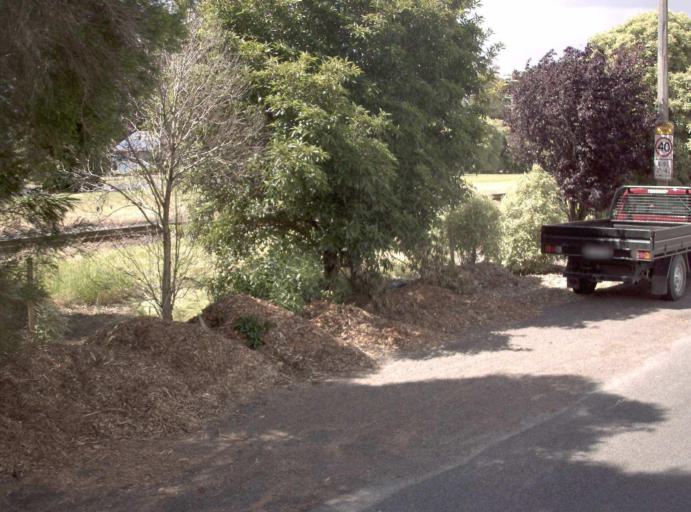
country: AU
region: Victoria
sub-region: Latrobe
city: Moe
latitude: -38.1790
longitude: 146.2535
